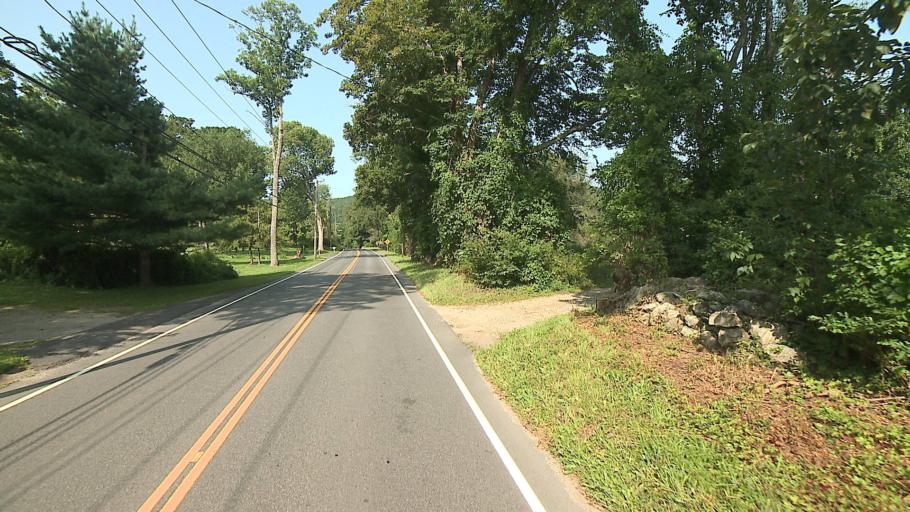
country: US
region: Connecticut
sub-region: Litchfield County
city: Kent
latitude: 41.7402
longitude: -73.4599
